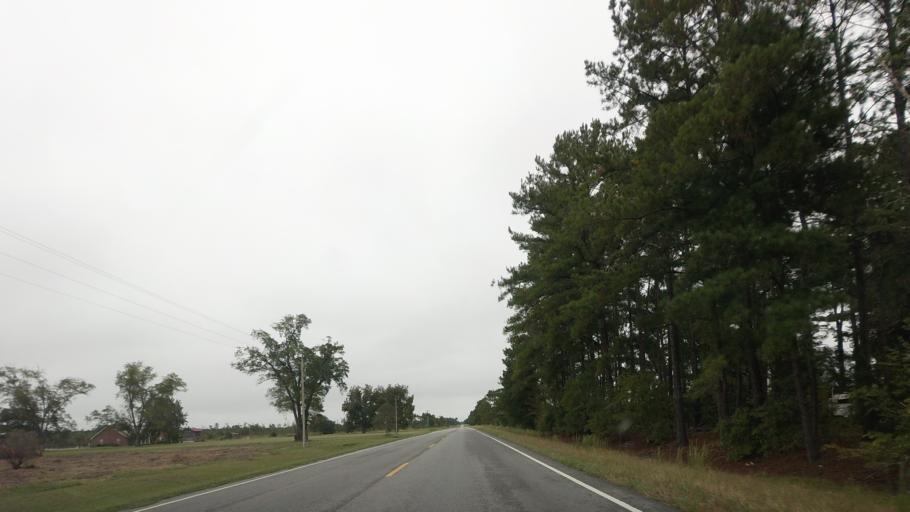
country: US
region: Georgia
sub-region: Berrien County
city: Nashville
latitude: 31.3124
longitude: -83.2320
